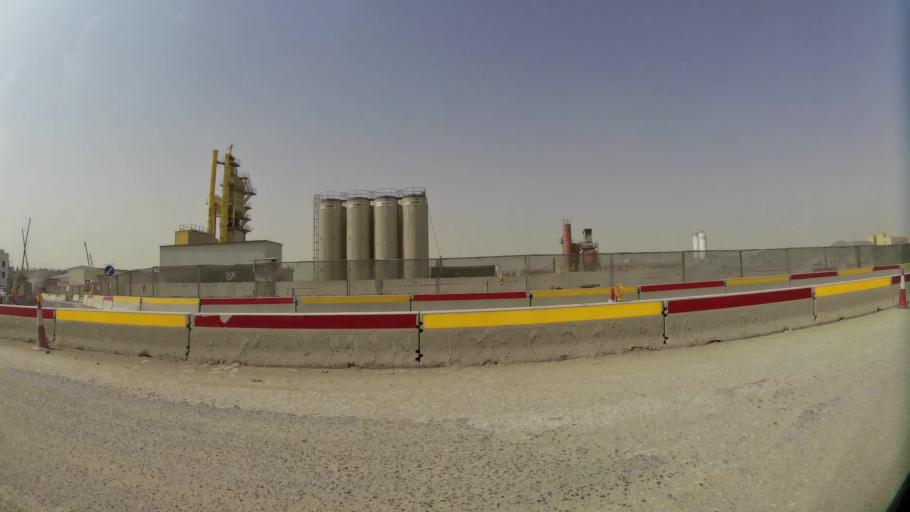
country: QA
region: Al Wakrah
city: Al Wukayr
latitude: 25.1771
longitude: 51.4452
